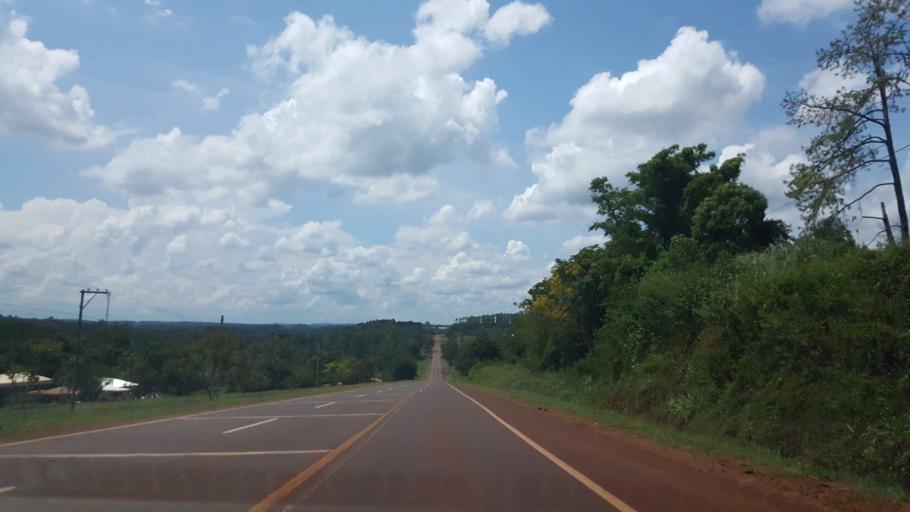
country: AR
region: Misiones
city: Garuhape
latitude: -26.8191
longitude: -54.9529
